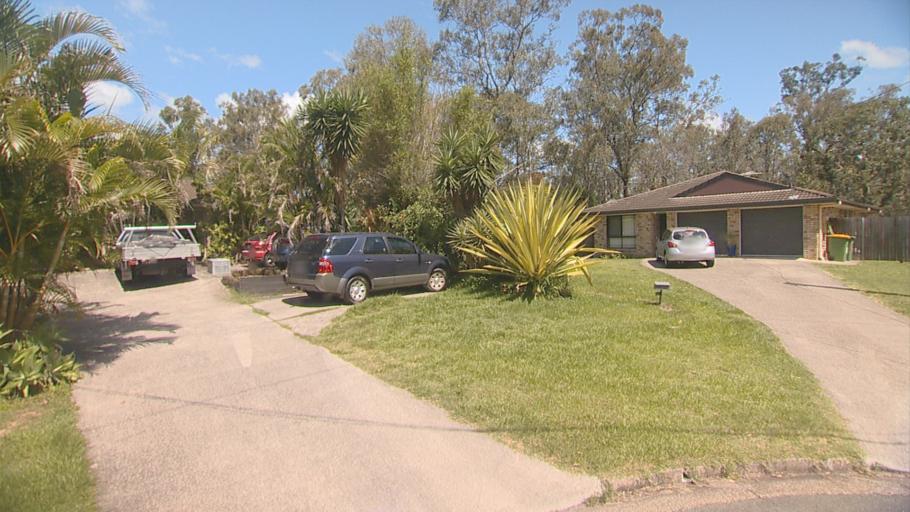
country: AU
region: Queensland
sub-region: Logan
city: Waterford West
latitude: -27.6942
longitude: 153.1606
